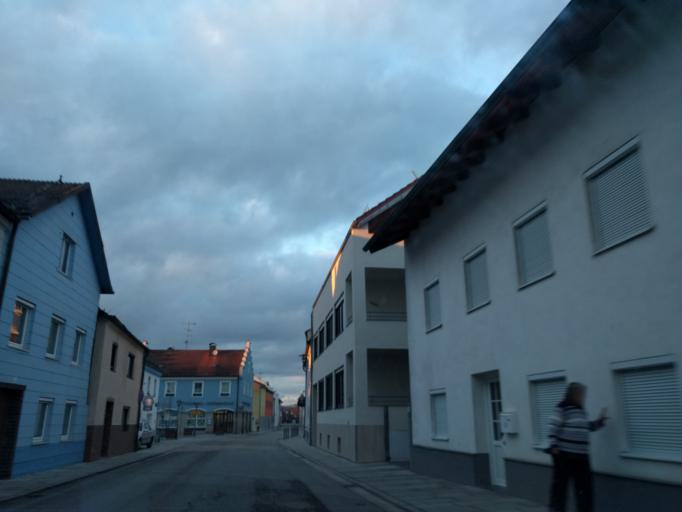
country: DE
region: Bavaria
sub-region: Lower Bavaria
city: Hofkirchen
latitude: 48.6775
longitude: 13.1185
